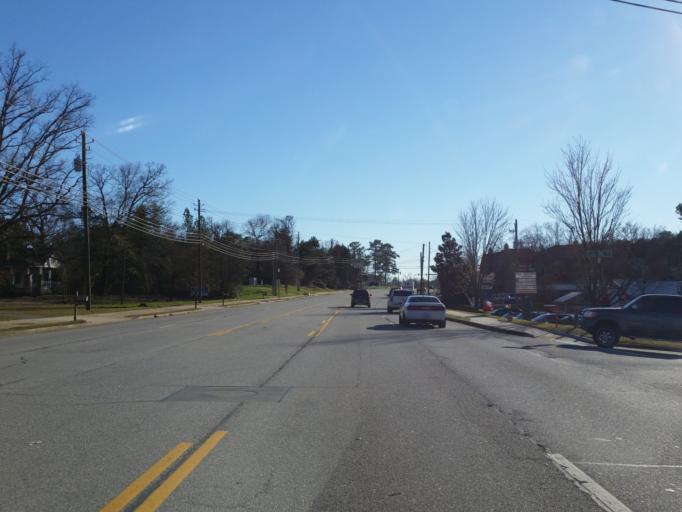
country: US
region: Georgia
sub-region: Cobb County
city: Vinings
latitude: 33.8569
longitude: -84.4921
